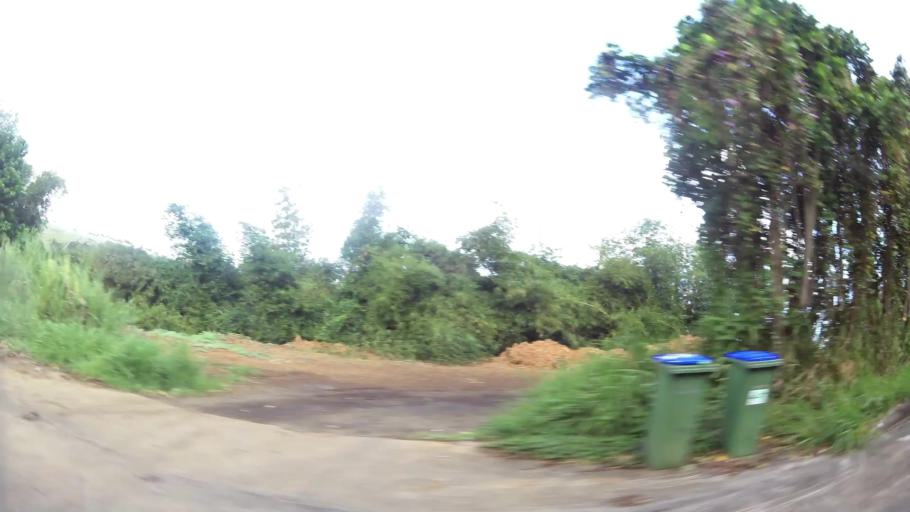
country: MQ
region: Martinique
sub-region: Martinique
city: Le Lorrain
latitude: 14.8259
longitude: -61.0389
